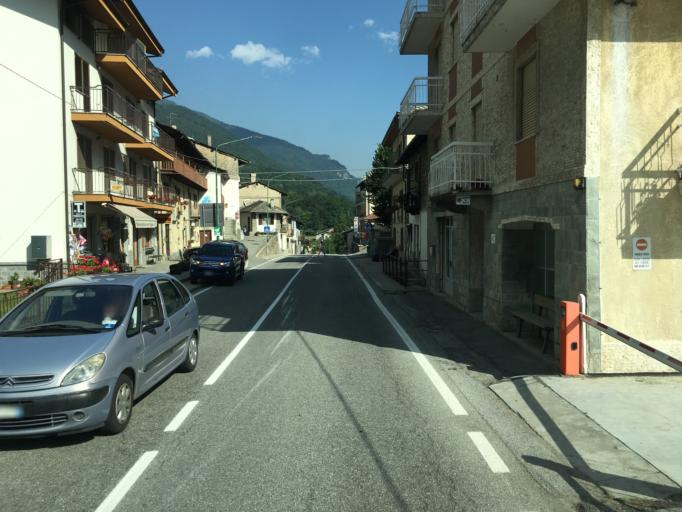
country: IT
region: Piedmont
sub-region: Provincia di Torino
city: Roure
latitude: 45.0174
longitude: 7.1131
